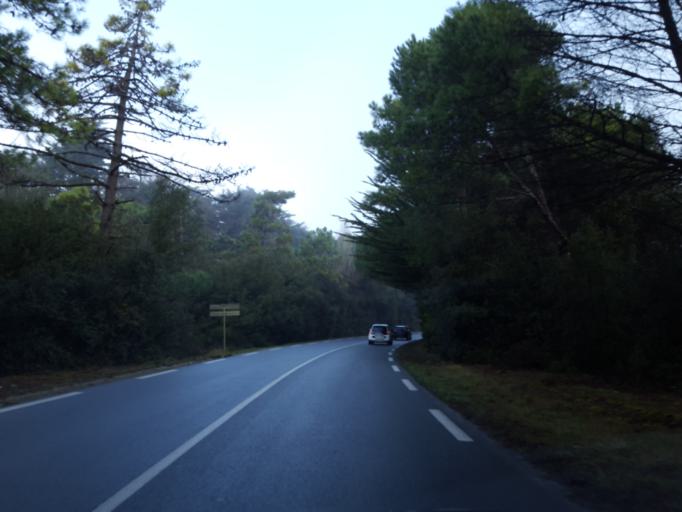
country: FR
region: Poitou-Charentes
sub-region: Departement de la Charente-Maritime
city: La Flotte
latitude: 46.1904
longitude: -1.3462
